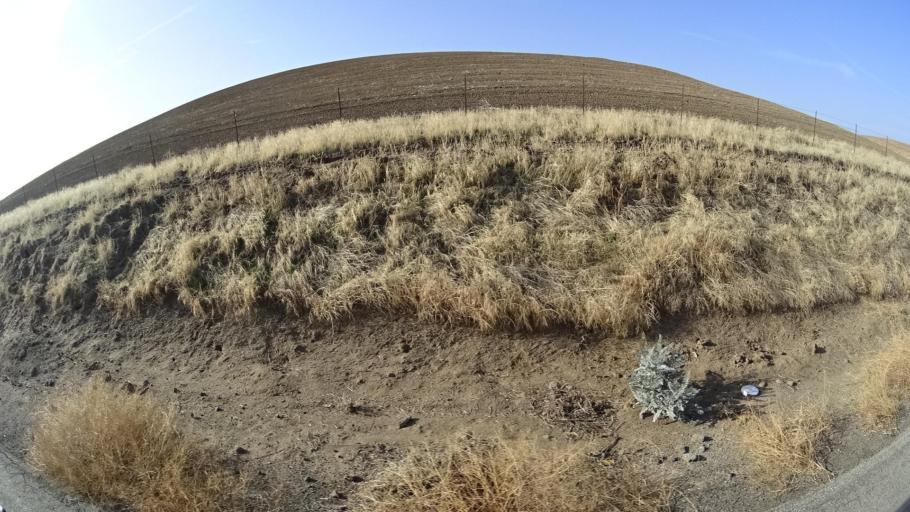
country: US
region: California
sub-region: Tulare County
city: Richgrove
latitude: 35.6564
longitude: -119.0698
